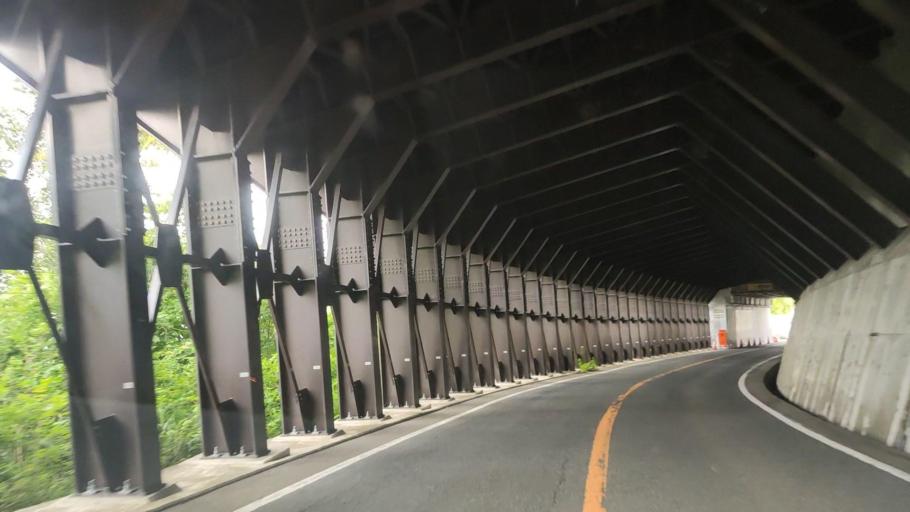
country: JP
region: Tottori
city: Yonago
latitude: 35.3643
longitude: 133.5217
